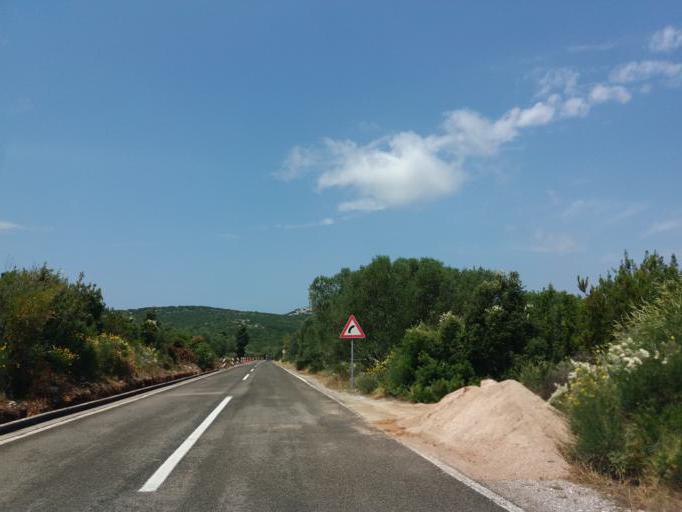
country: HR
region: Zadarska
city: Sali
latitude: 43.9802
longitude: 15.0804
